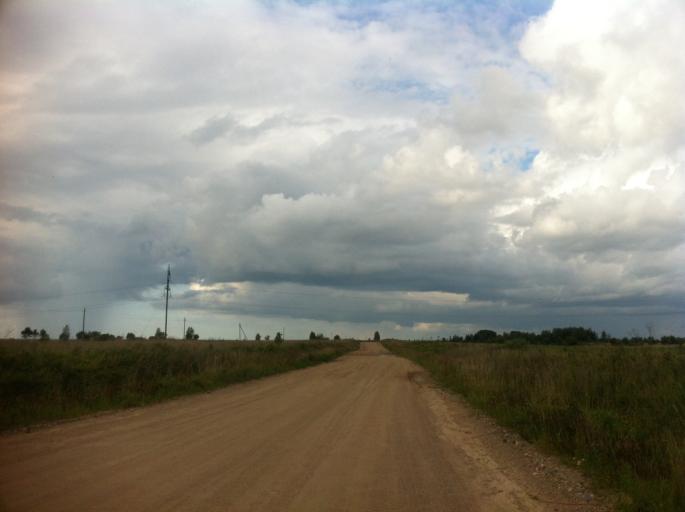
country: RU
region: Pskov
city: Izborsk
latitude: 57.8287
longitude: 27.9823
